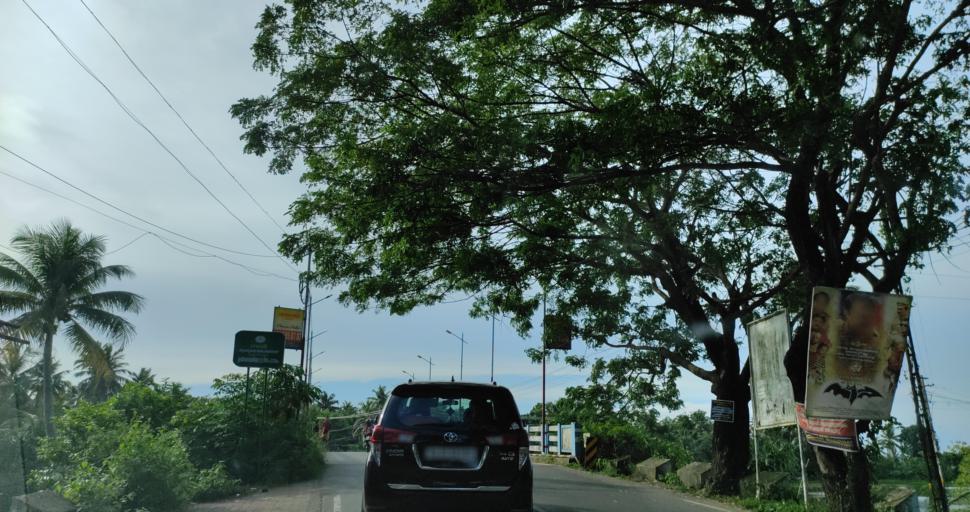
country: IN
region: Kerala
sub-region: Alappuzha
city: Shertallai
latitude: 9.6481
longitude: 76.4307
